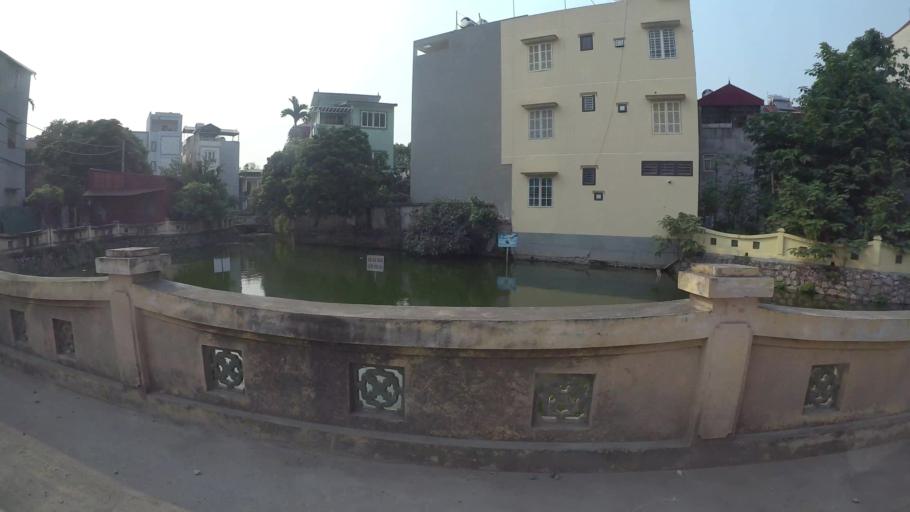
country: VN
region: Ha Noi
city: Cau Dien
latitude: 21.0007
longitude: 105.7458
